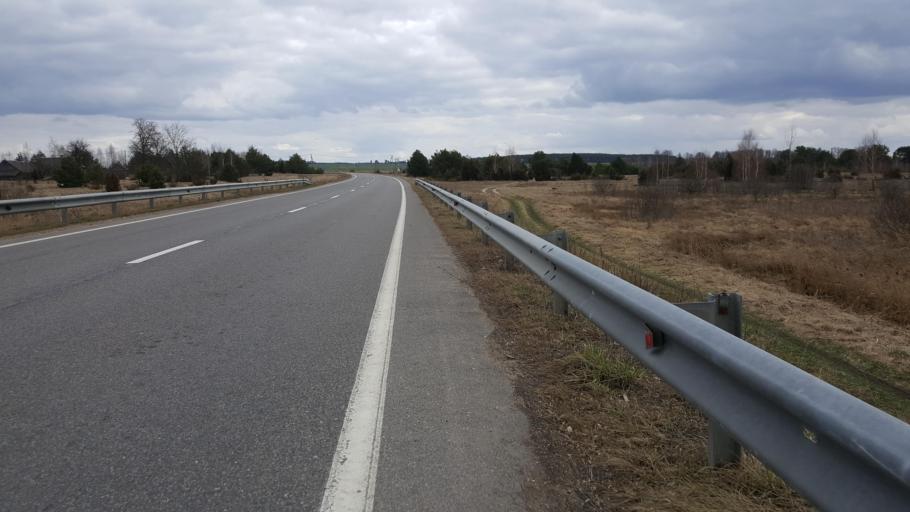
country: BY
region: Brest
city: Kamyanyets
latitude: 52.4258
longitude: 23.8381
